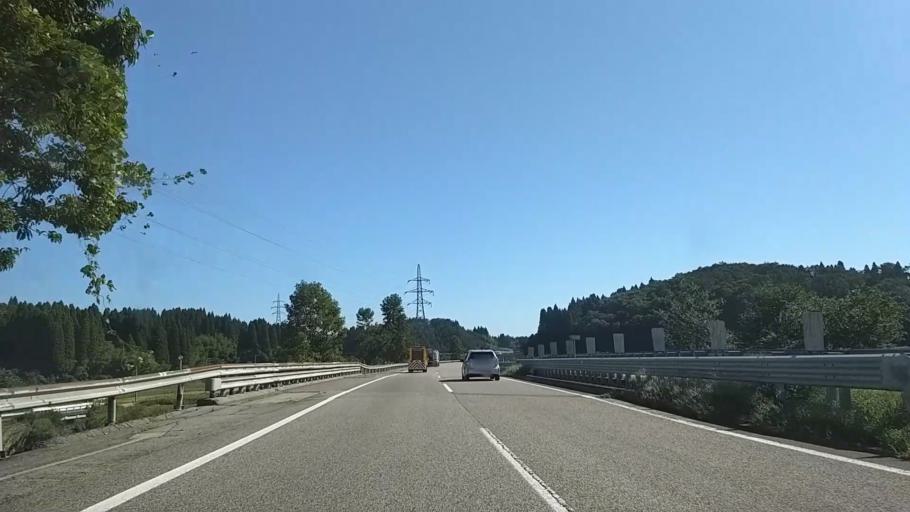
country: JP
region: Toyama
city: Takaoka
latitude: 36.6873
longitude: 137.0588
